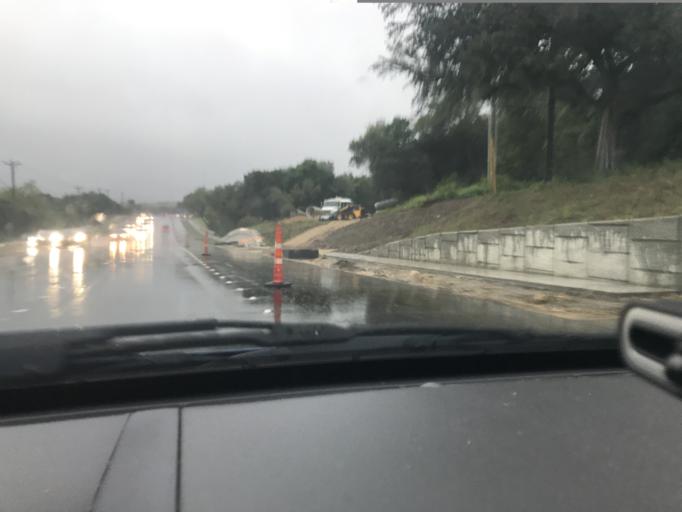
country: US
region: Texas
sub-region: Travis County
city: West Lake Hills
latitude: 30.2879
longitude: -97.8156
